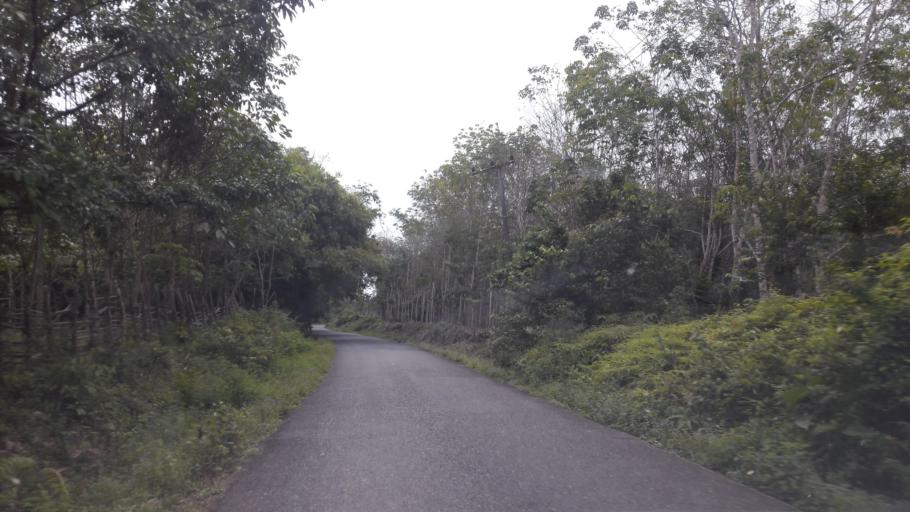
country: ID
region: South Sumatra
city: Gunungmenang
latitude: -3.1194
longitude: 104.0945
